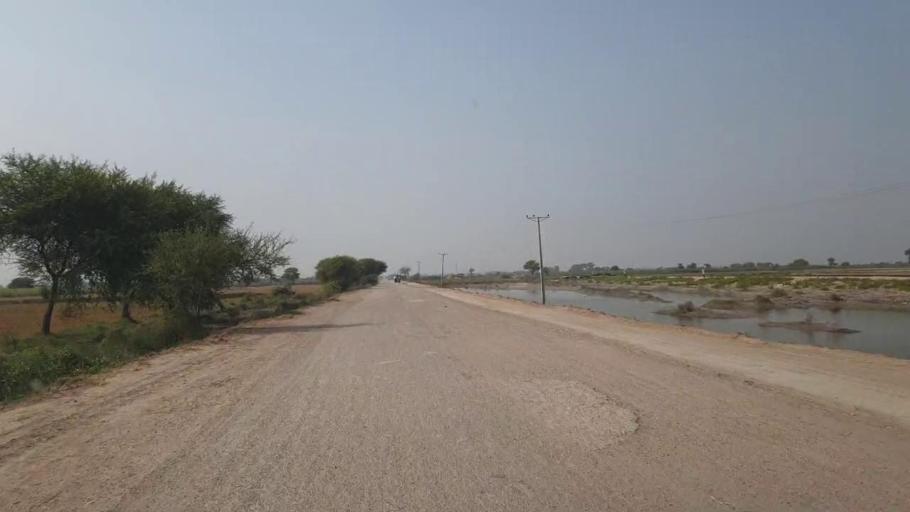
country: PK
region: Sindh
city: Matli
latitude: 25.0259
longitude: 68.6739
